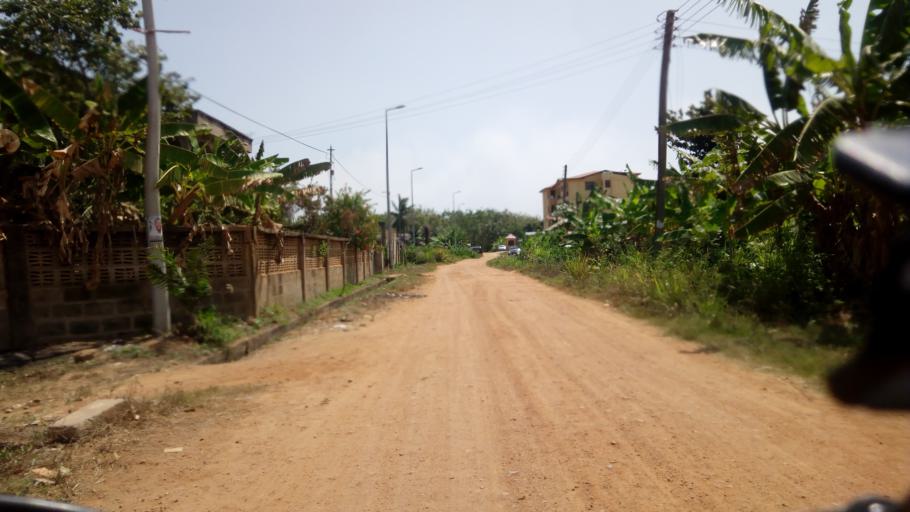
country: GH
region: Central
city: Cape Coast
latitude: 5.1330
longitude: -1.2807
